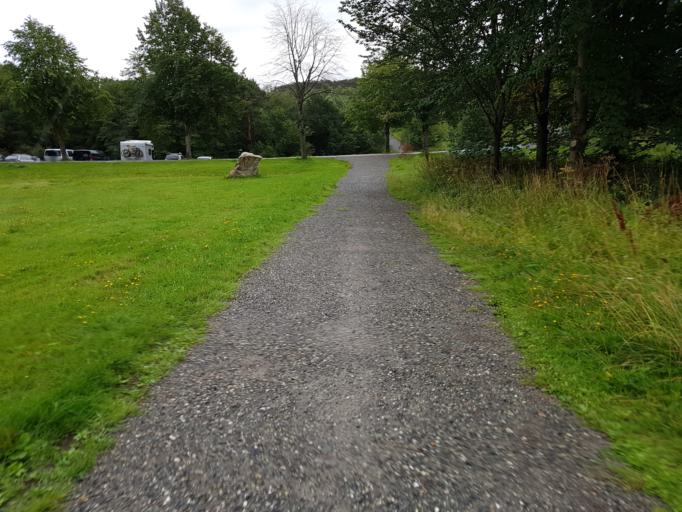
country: NO
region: Sor-Trondelag
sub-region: Trondheim
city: Trondheim
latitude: 63.4383
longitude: 10.4700
